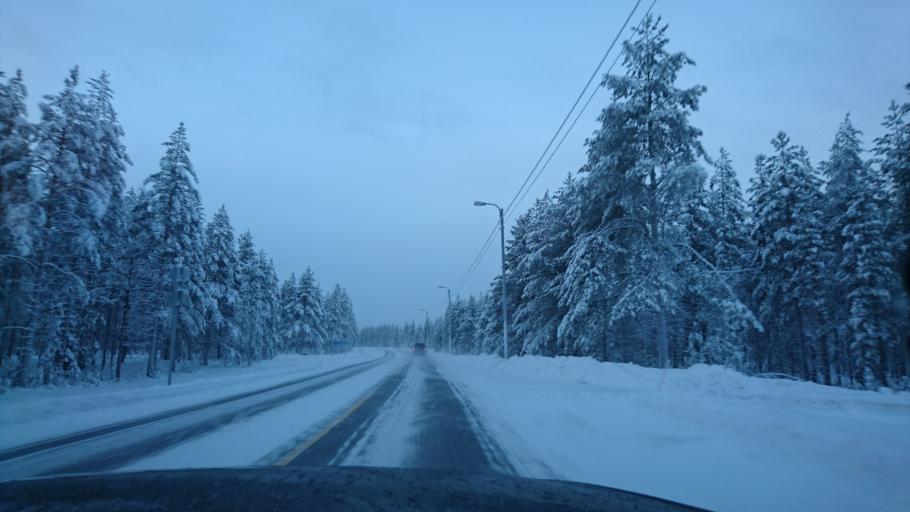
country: FI
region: Kainuu
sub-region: Kehys-Kainuu
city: Puolanka
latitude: 65.4298
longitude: 27.5263
